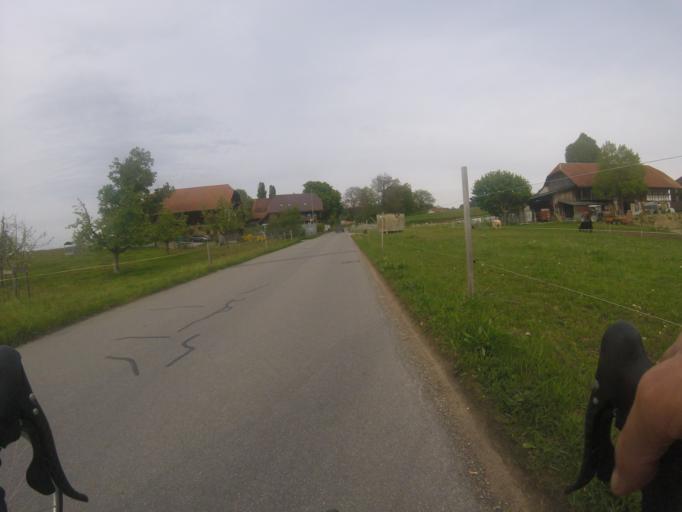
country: CH
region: Bern
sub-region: Bern-Mittelland District
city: Niederwichtrach
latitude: 46.8401
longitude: 7.5920
